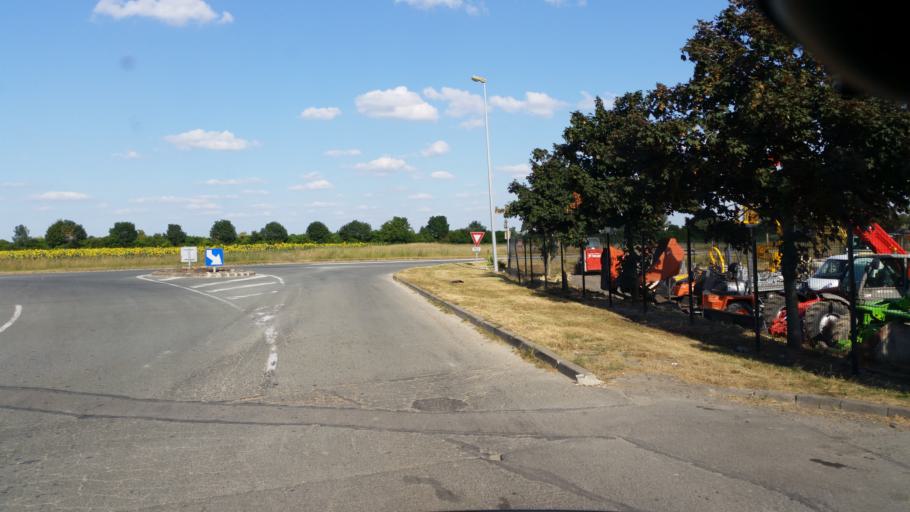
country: FR
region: Poitou-Charentes
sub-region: Departement de la Charente-Maritime
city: Saint-Jean-de-Liversay
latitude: 46.2299
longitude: -0.8807
